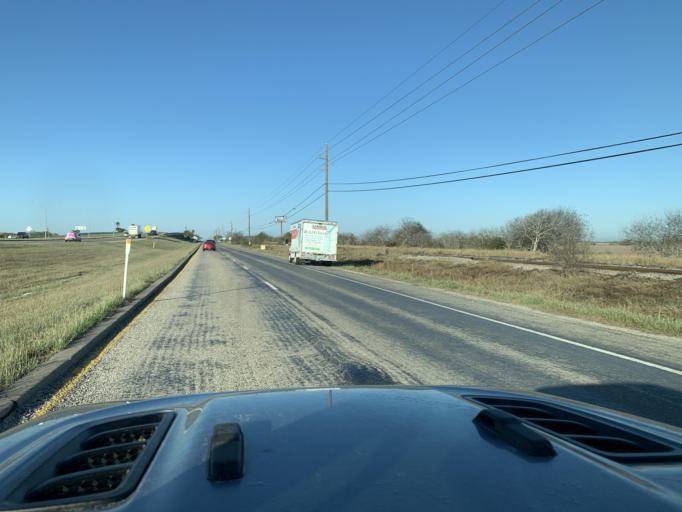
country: US
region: Texas
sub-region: Nueces County
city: Corpus Christi
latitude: 27.7853
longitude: -97.4977
